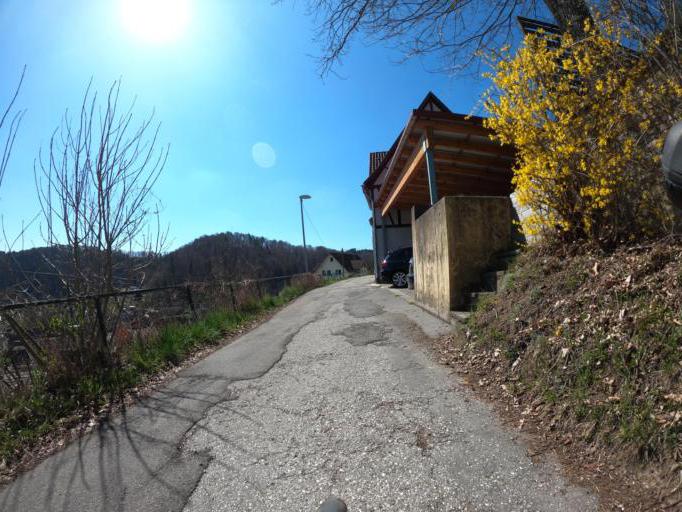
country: DE
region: Baden-Wuerttemberg
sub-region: Karlsruhe Region
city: Empfingen
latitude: 48.4206
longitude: 8.7573
